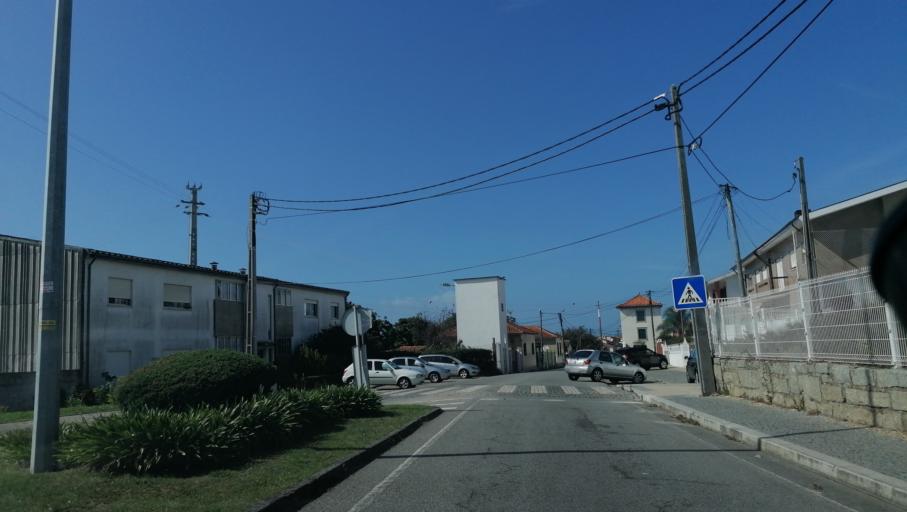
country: PT
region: Aveiro
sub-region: Espinho
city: Silvalde
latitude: 40.9982
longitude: -8.6165
